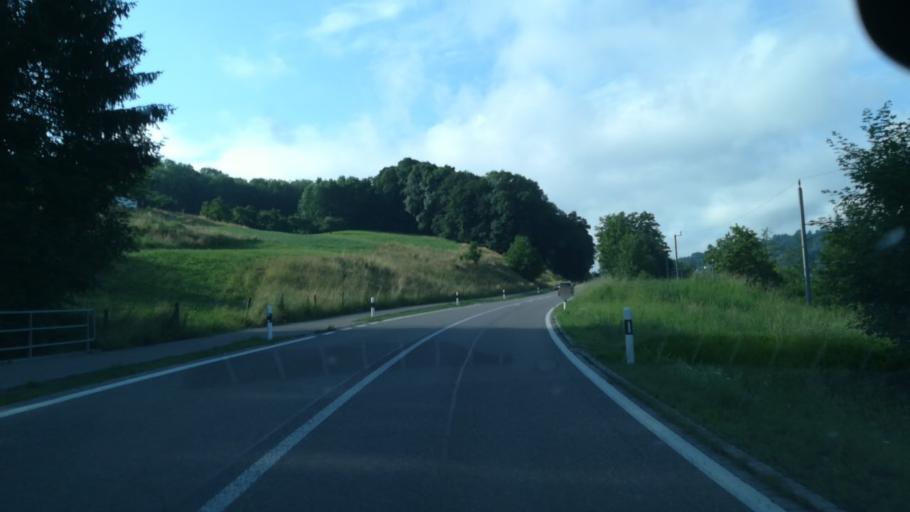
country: CH
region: Thurgau
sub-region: Weinfelden District
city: Sulgen
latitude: 47.5174
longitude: 9.2096
